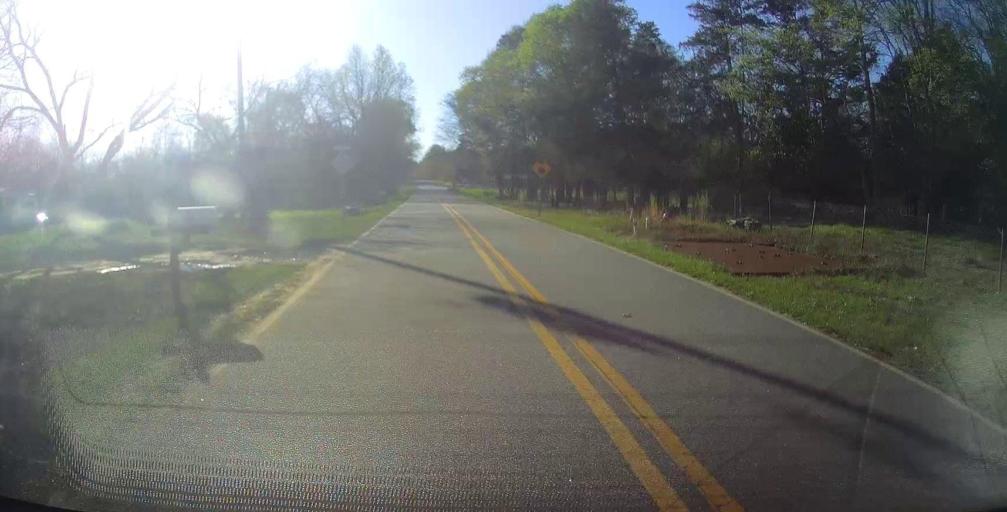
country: US
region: Georgia
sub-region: Houston County
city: Perry
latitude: 32.3640
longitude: -83.6640
